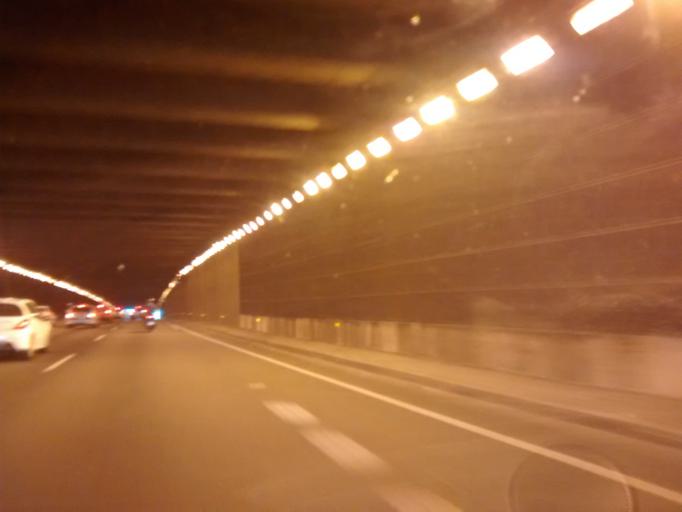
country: ES
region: Catalonia
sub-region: Provincia de Barcelona
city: L'Hospitalet de Llobregat
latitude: 41.3643
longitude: 2.0897
